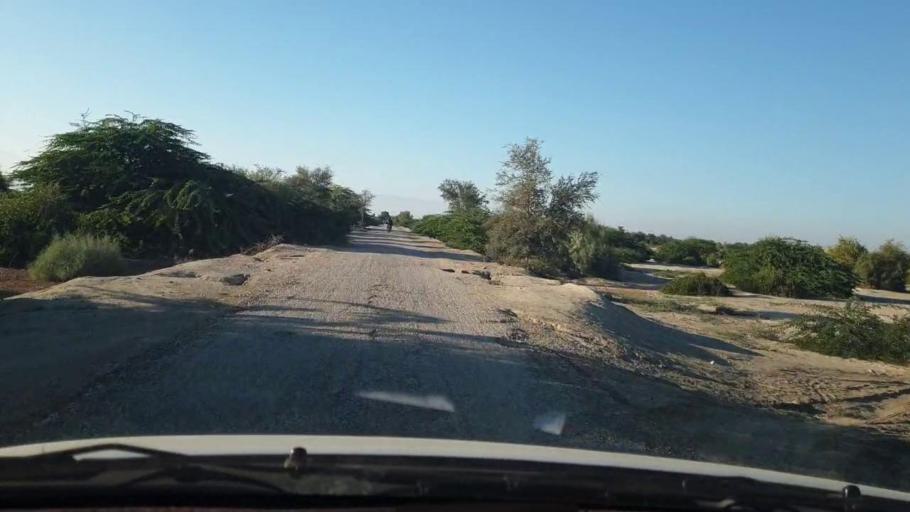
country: PK
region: Sindh
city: Johi
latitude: 26.7718
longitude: 67.4571
